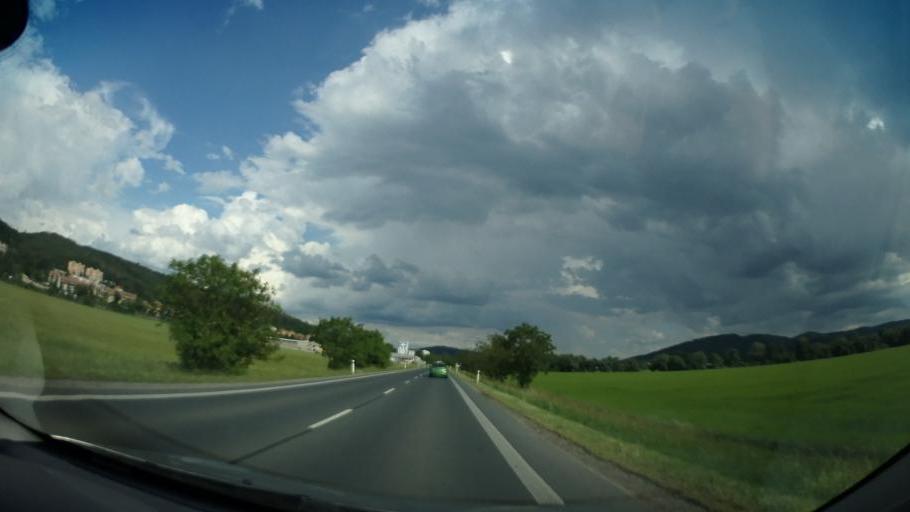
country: CZ
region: South Moravian
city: Tisnov
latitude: 49.3385
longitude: 16.4257
